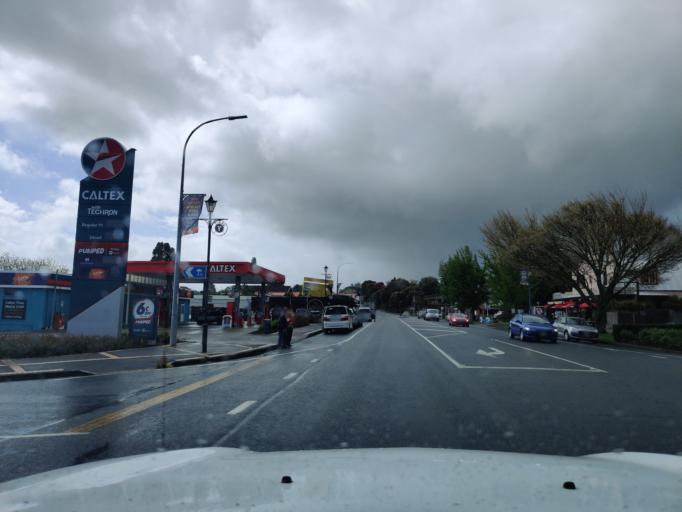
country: NZ
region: Waikato
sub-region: Matamata-Piako District
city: Matamata
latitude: -37.9773
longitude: 175.7565
